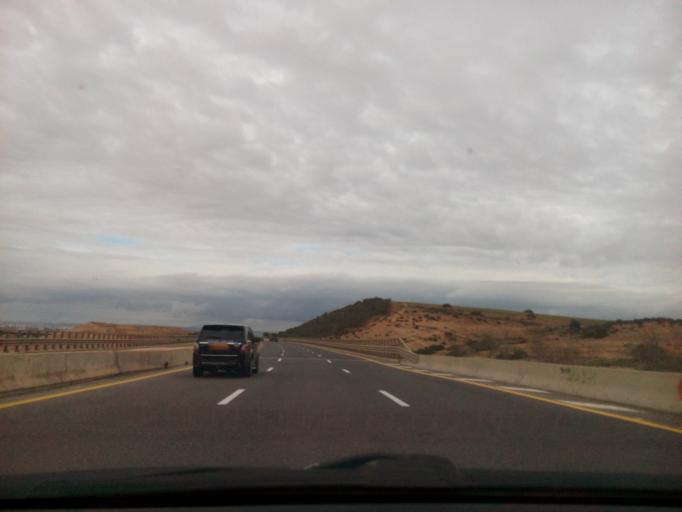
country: DZ
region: Sidi Bel Abbes
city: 'Ain el Berd
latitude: 35.4802
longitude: -0.3848
